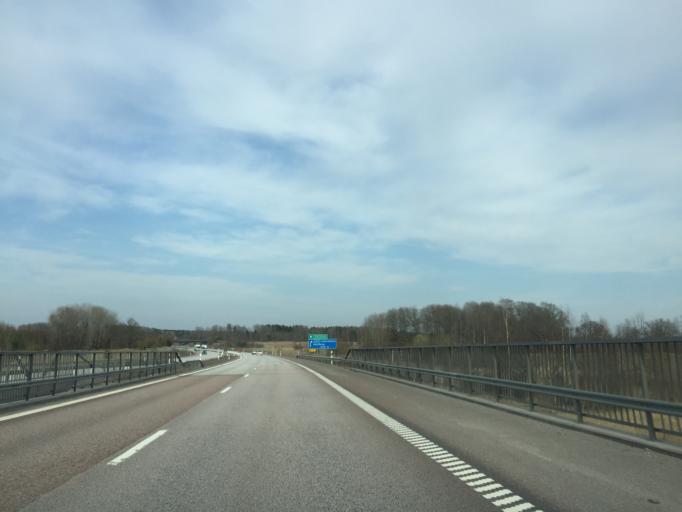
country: SE
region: Vaestmanland
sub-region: Arboga Kommun
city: Arboga
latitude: 59.4065
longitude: 15.7594
